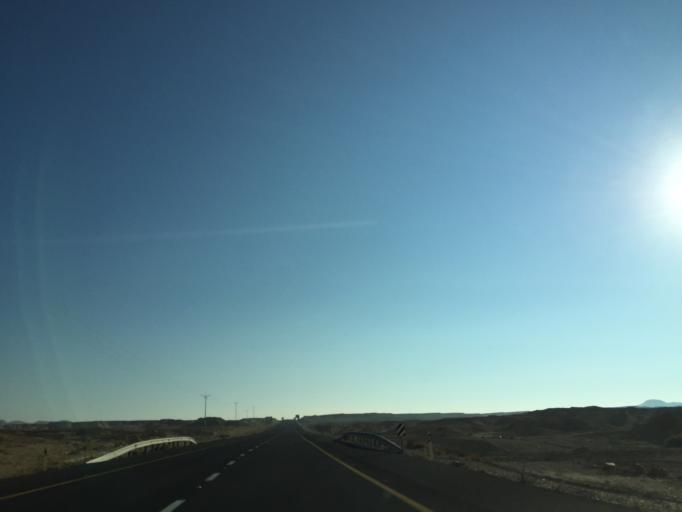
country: IL
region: Southern District
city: Mitzpe Ramon
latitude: 30.2781
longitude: 35.0090
